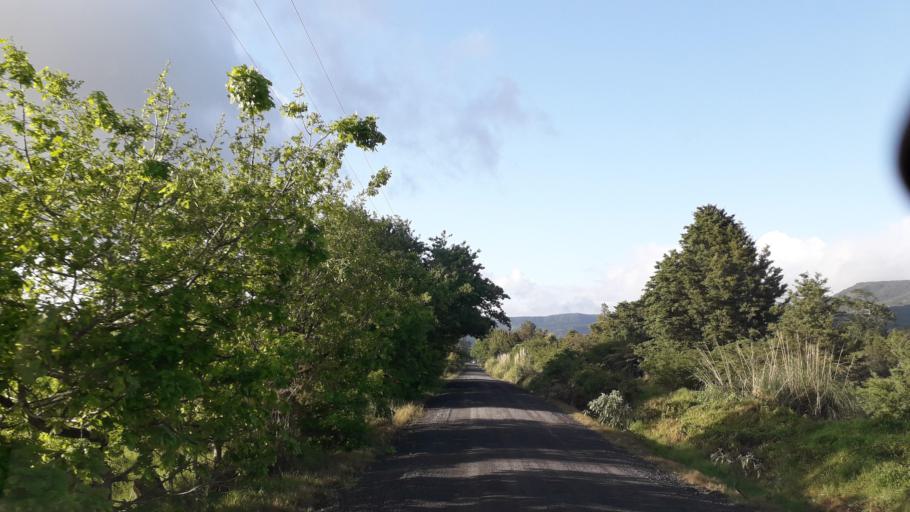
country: NZ
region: Northland
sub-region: Far North District
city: Waimate North
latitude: -35.4940
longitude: 173.6996
